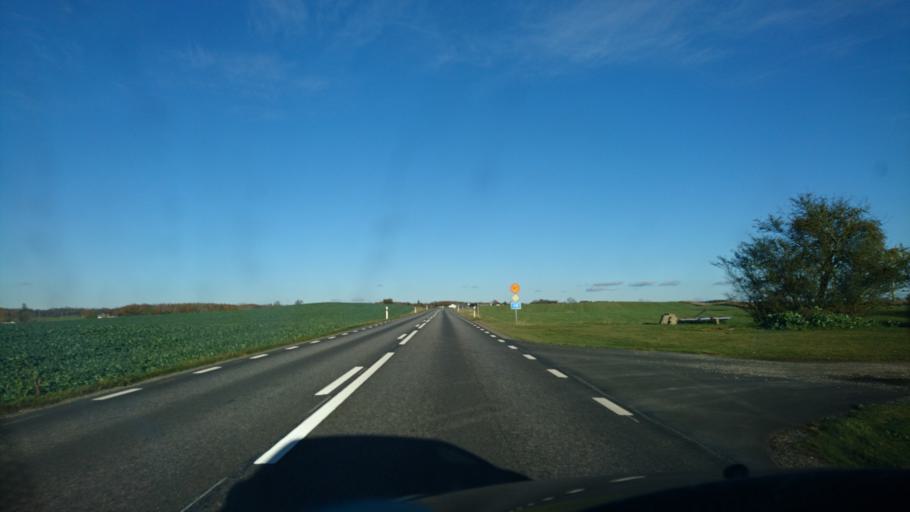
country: SE
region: Skane
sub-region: Tomelilla Kommun
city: Tomelilla
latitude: 55.5894
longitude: 13.9737
